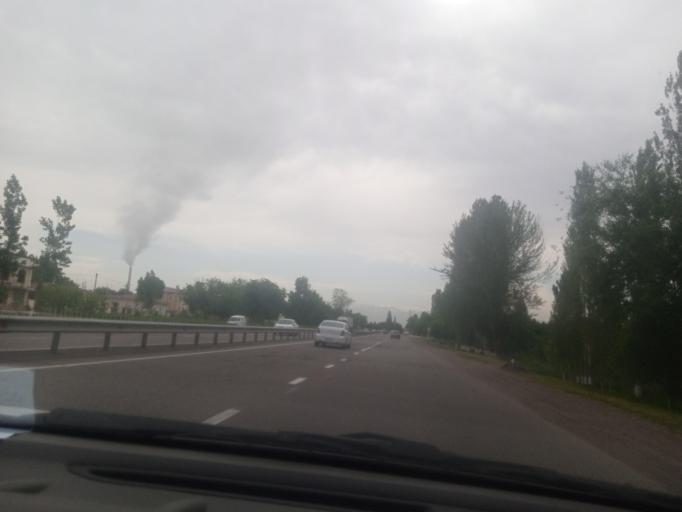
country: UZ
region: Toshkent
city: Ohangaron
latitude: 40.9084
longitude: 69.7652
